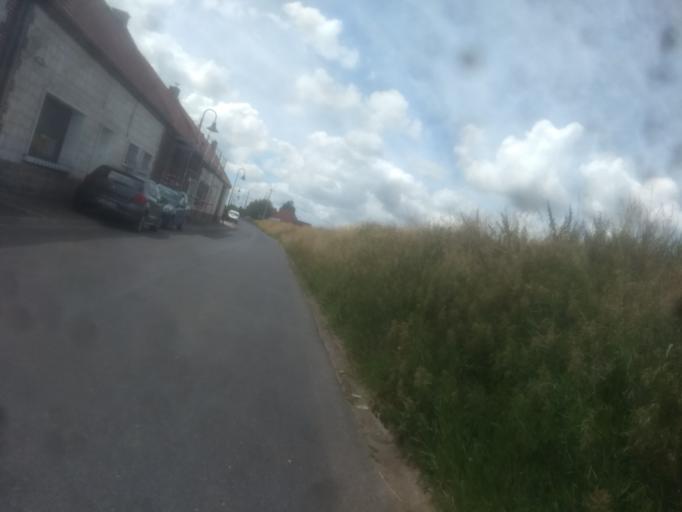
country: FR
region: Nord-Pas-de-Calais
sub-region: Departement du Pas-de-Calais
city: Mont-Saint-Eloi
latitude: 50.3447
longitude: 2.6742
